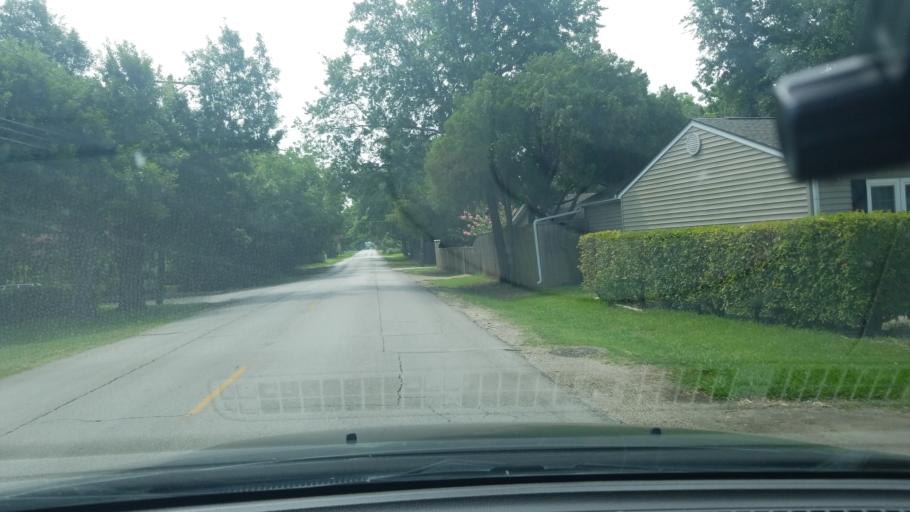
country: US
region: Texas
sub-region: Dallas County
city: Highland Park
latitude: 32.8206
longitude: -96.7118
